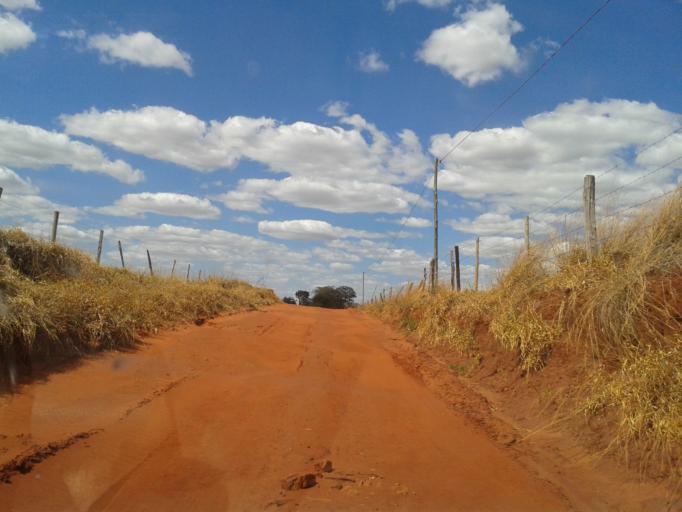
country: BR
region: Minas Gerais
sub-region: Monte Alegre De Minas
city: Monte Alegre de Minas
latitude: -18.7768
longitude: -49.0844
